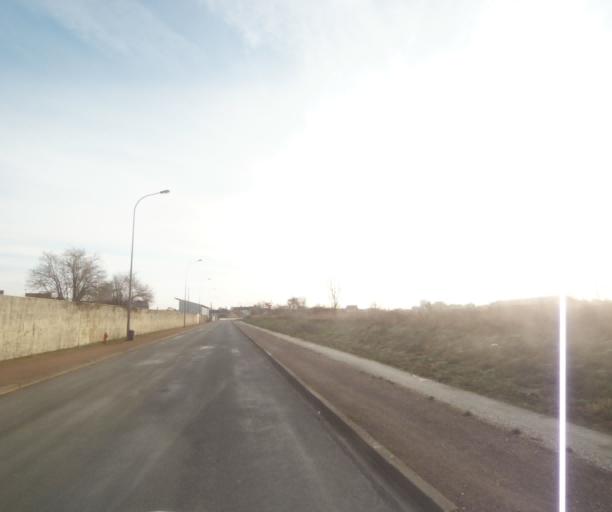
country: FR
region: Champagne-Ardenne
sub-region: Departement de la Haute-Marne
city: Saint-Dizier
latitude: 48.6455
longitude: 4.9410
